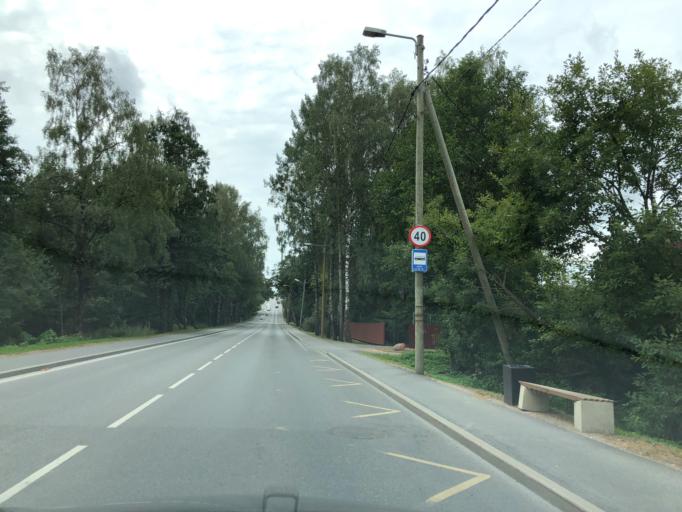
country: EE
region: Harju
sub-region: Saue vald
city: Laagri
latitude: 59.3900
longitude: 24.6420
